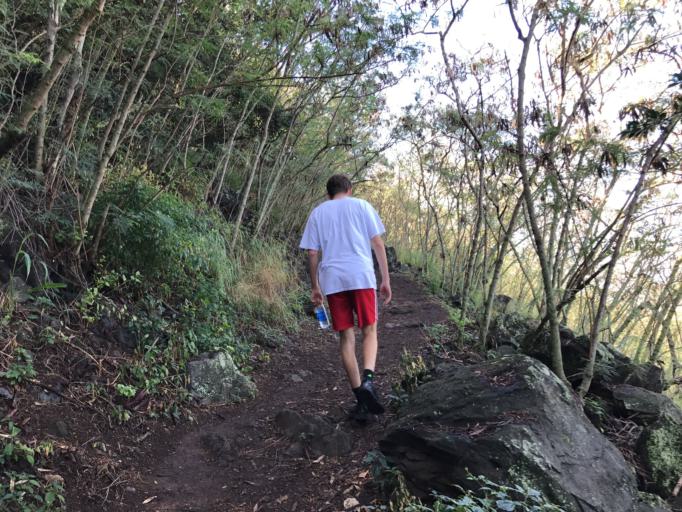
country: US
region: Hawaii
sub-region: Honolulu County
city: Mokuleia
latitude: 21.5735
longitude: -158.2071
